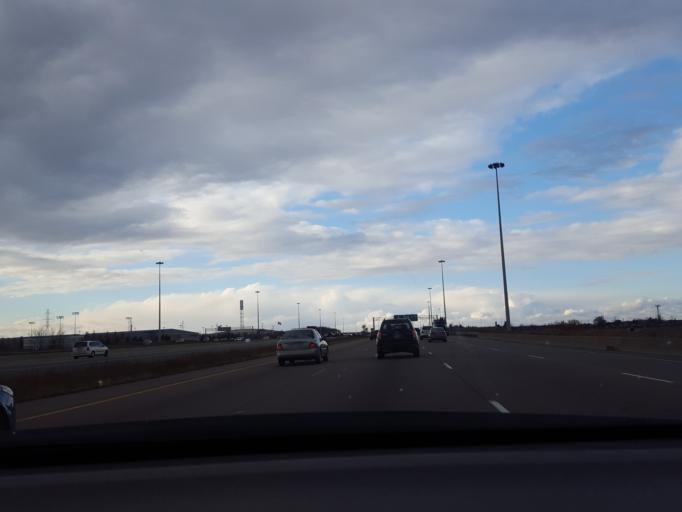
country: CA
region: Ontario
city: Mississauga
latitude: 43.6262
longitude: -79.6417
